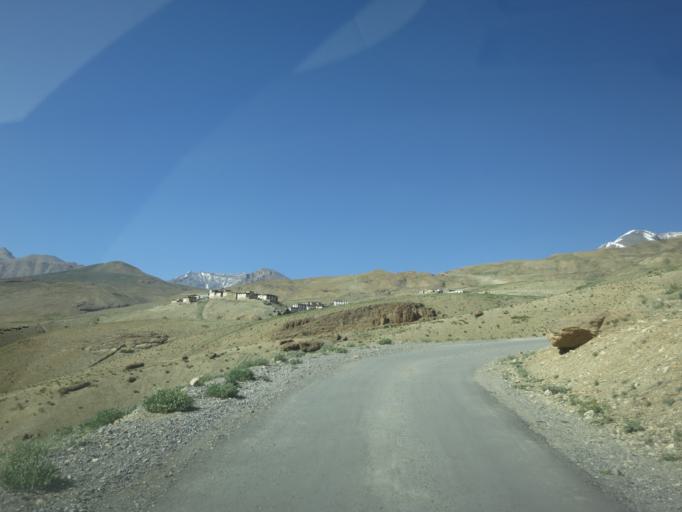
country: IN
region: Himachal Pradesh
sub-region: Kulu
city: Manali
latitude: 32.3255
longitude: 78.0044
